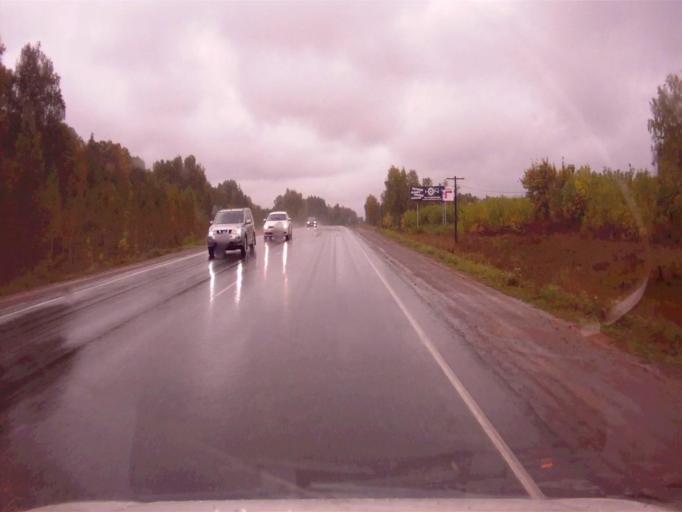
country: RU
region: Chelyabinsk
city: Argayash
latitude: 55.4687
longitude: 60.9062
